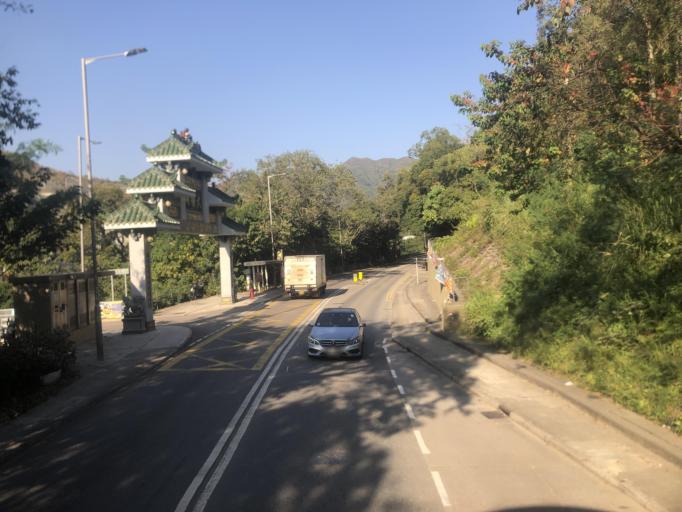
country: CN
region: Guangdong
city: Liantang
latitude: 22.5198
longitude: 114.1763
